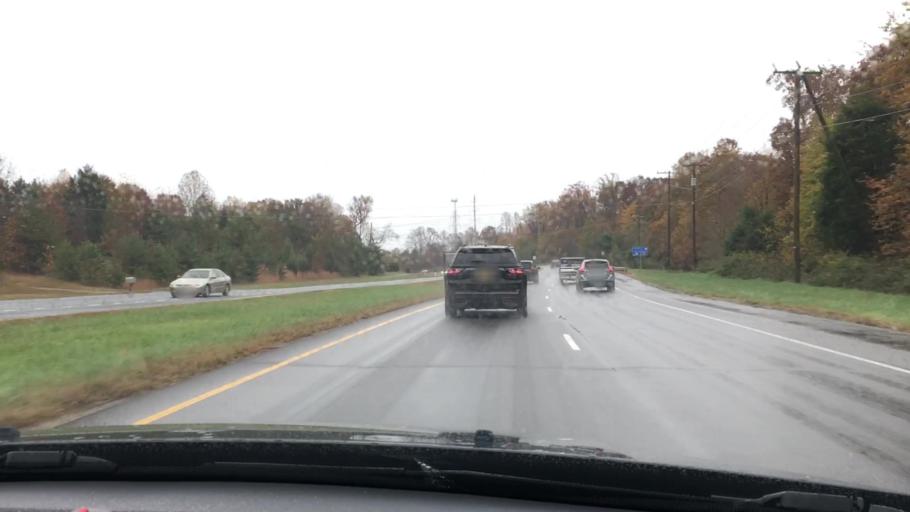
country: US
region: Virginia
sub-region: Fairfax County
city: Burke
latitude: 38.7417
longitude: -77.2869
